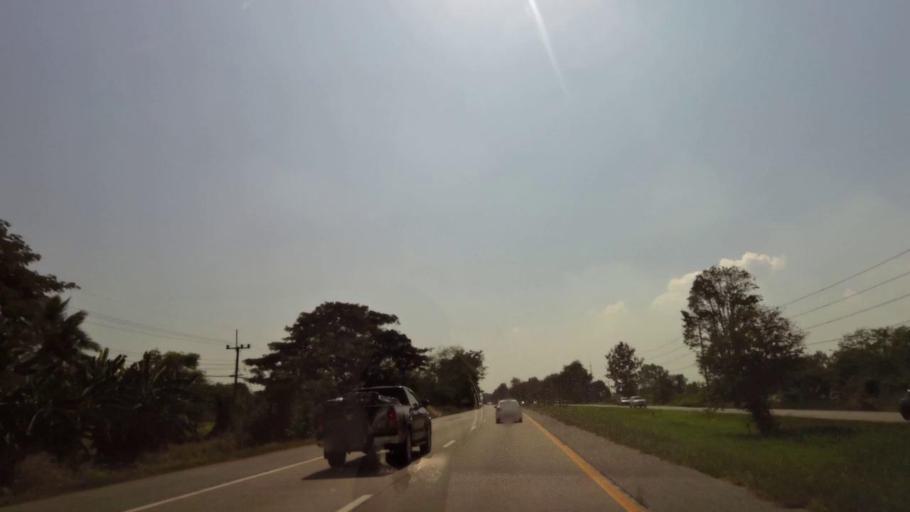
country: TH
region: Phichit
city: Wachira Barami
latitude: 16.5891
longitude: 100.1469
